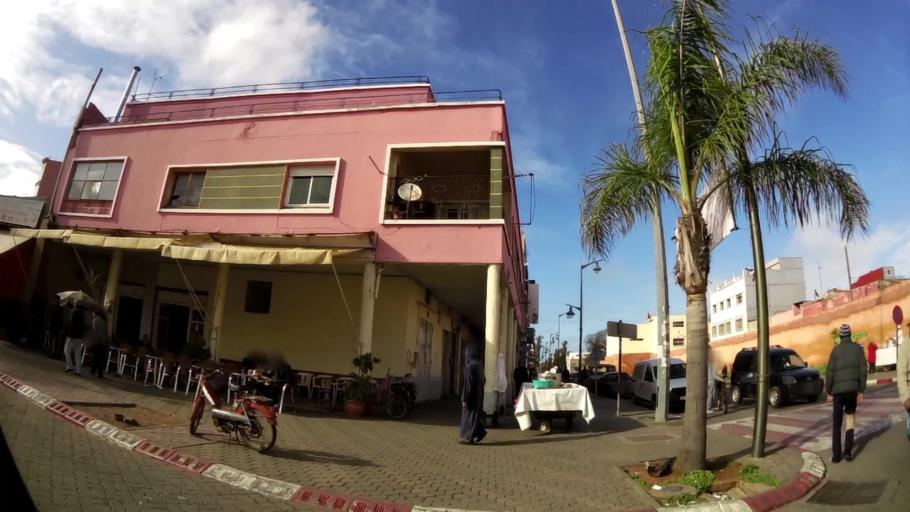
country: MA
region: Grand Casablanca
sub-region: Mohammedia
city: Mohammedia
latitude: 33.6994
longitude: -7.3885
